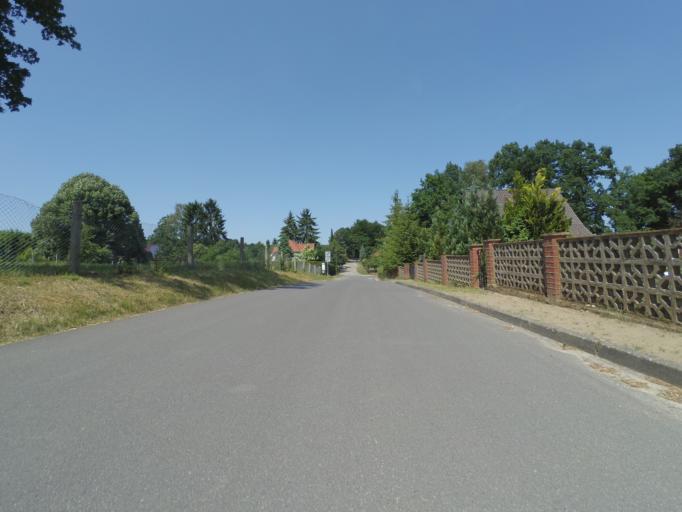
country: DE
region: Mecklenburg-Vorpommern
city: Plau am See
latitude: 53.4347
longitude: 12.2819
